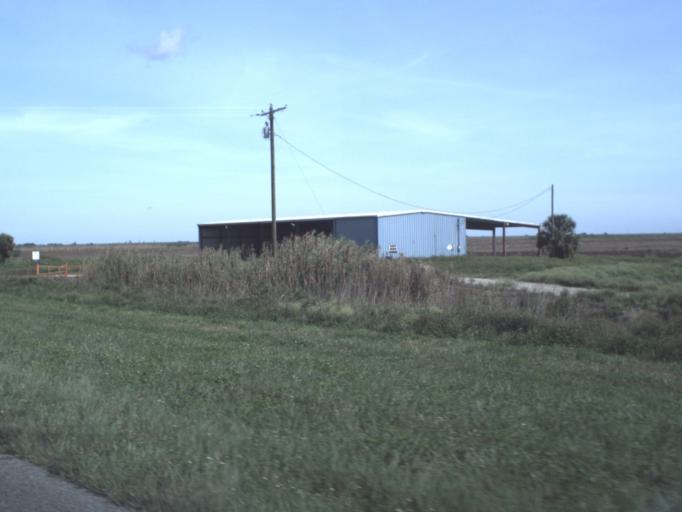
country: US
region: Florida
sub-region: Glades County
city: Moore Haven
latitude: 26.7878
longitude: -81.0826
